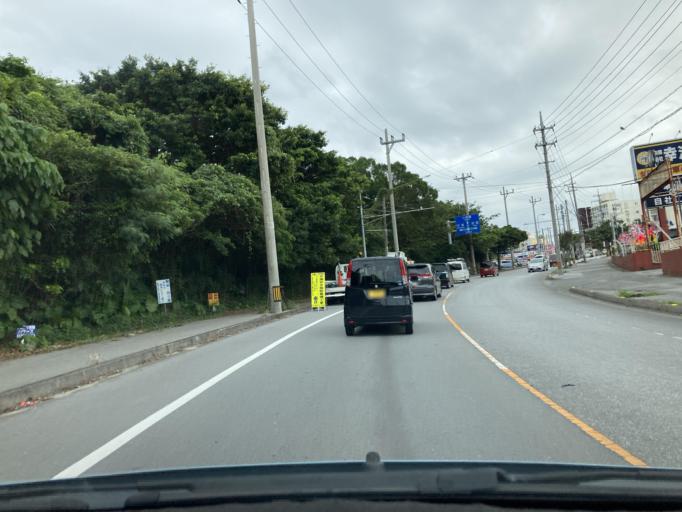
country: JP
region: Okinawa
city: Ginowan
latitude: 26.2445
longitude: 127.7645
